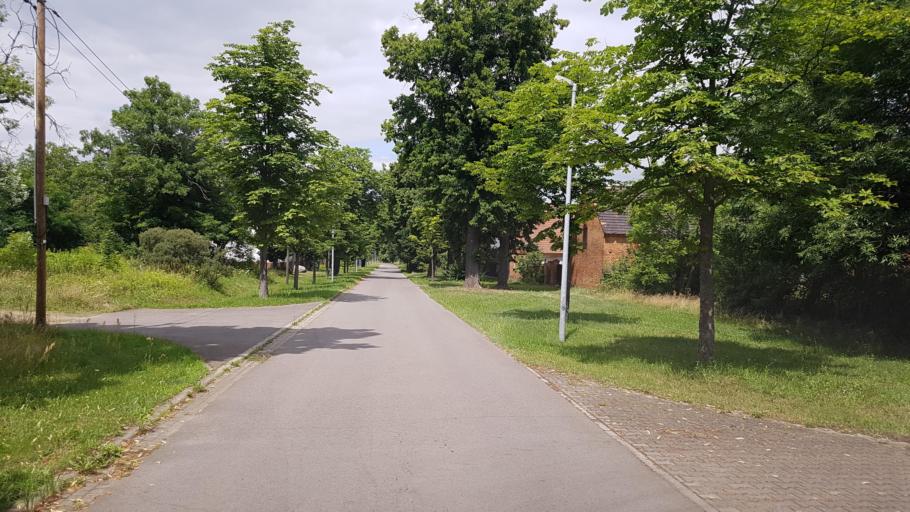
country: DE
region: Brandenburg
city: Altdobern
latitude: 51.6491
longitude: 14.0804
